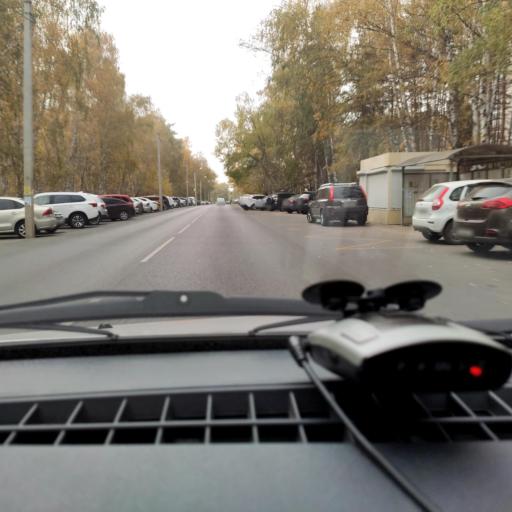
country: RU
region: Voronezj
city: Podgornoye
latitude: 51.7389
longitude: 39.1774
